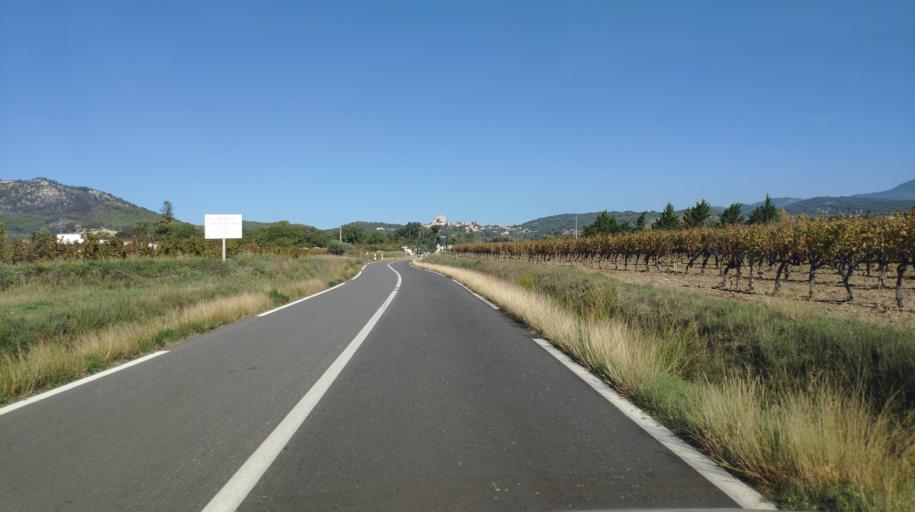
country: FR
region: Provence-Alpes-Cote d'Azur
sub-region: Departement du Vaucluse
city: Caromb
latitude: 44.1171
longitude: 5.0843
